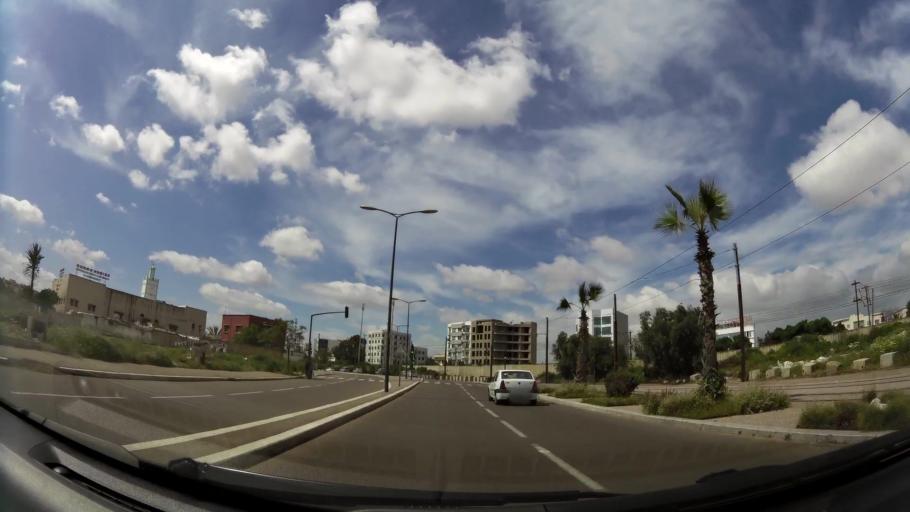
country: MA
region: Grand Casablanca
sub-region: Casablanca
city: Casablanca
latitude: 33.5604
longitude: -7.6282
